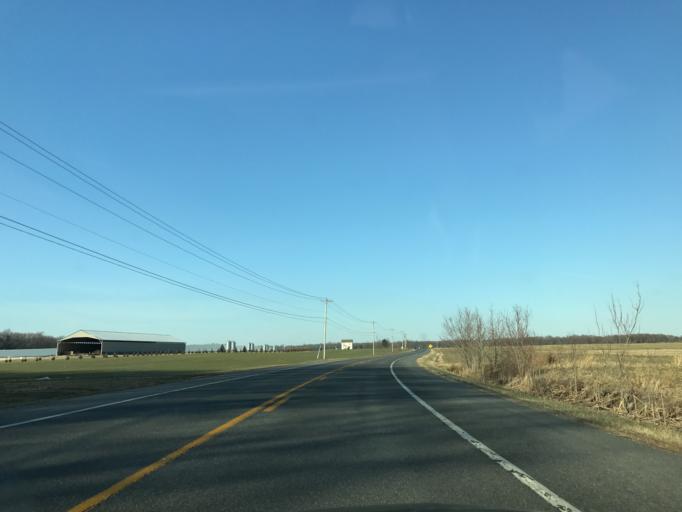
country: US
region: Maryland
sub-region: Caroline County
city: Greensboro
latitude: 39.1540
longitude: -75.8663
